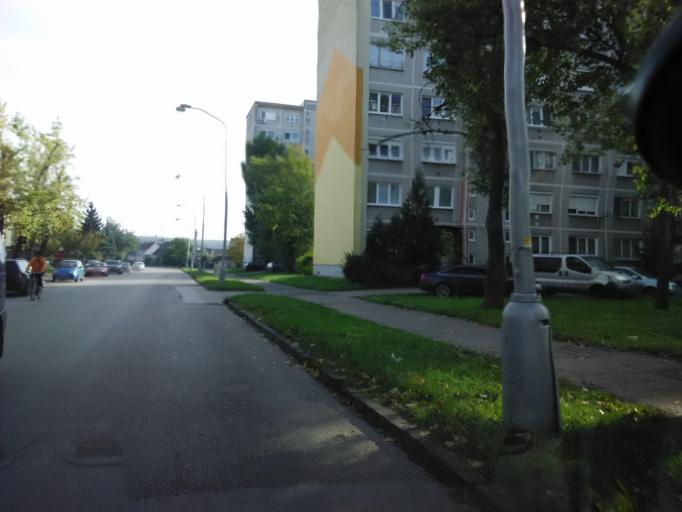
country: SK
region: Nitriansky
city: Komarno
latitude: 47.7684
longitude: 18.1291
